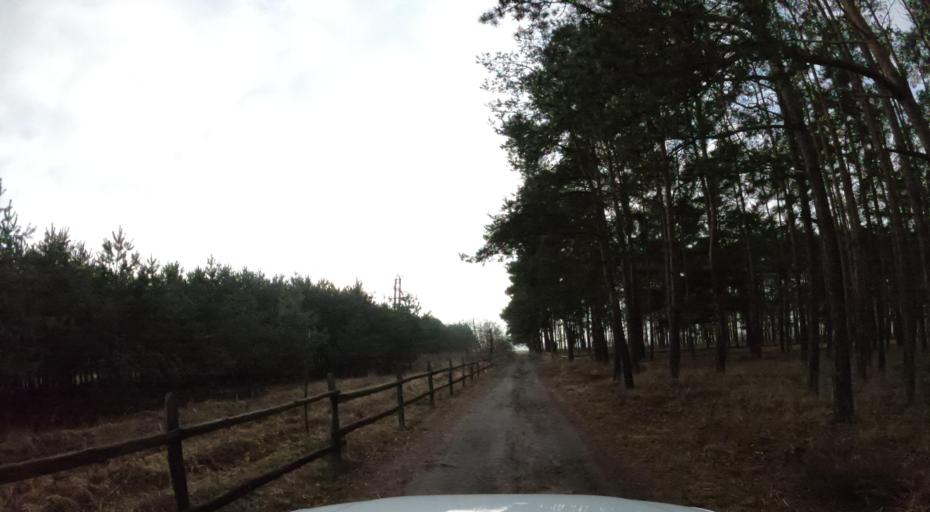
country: DE
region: Brandenburg
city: Manschnow
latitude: 52.6362
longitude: 14.5543
